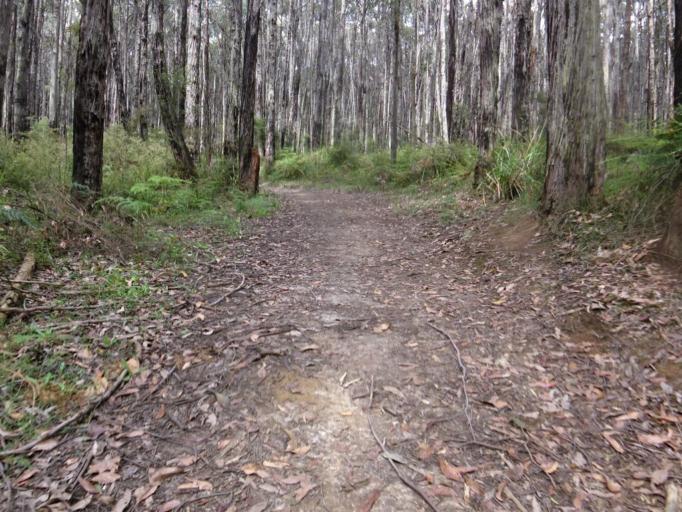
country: AU
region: Victoria
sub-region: Cardinia
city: Cockatoo
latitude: -37.9330
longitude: 145.4744
